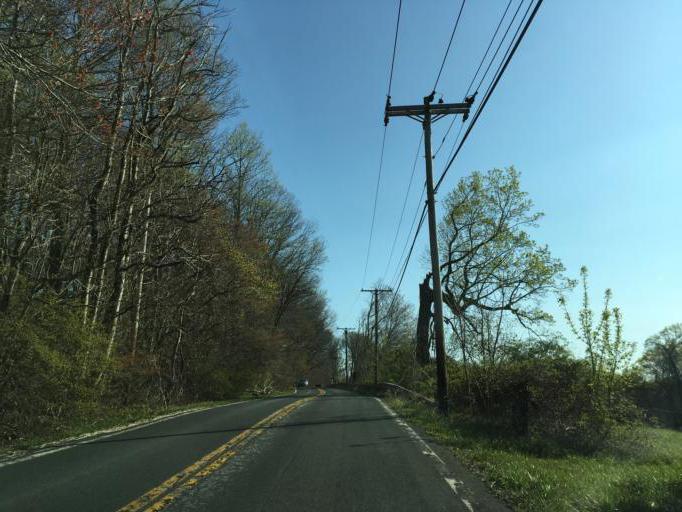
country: US
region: Maryland
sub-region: Baltimore County
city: Perry Hall
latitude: 39.4526
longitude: -76.4948
